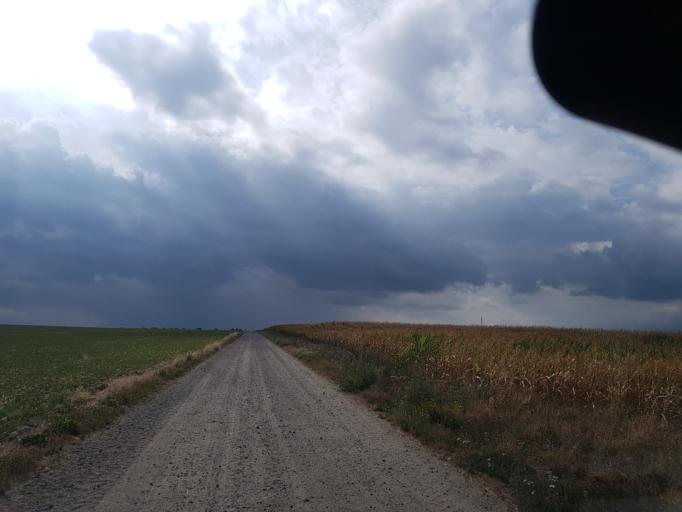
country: DE
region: Brandenburg
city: Treuenbrietzen
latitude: 52.0098
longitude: 12.8377
